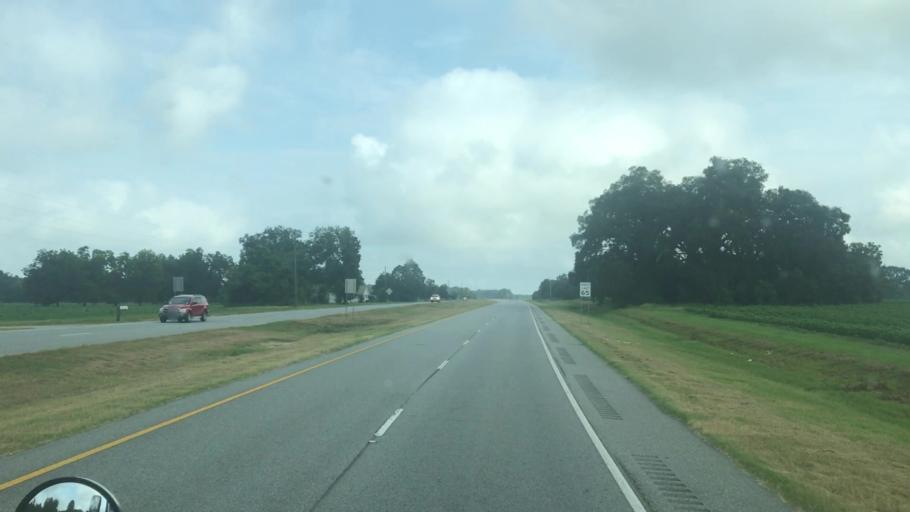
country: US
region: Georgia
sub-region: Miller County
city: Colquitt
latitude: 31.1763
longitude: -84.7601
